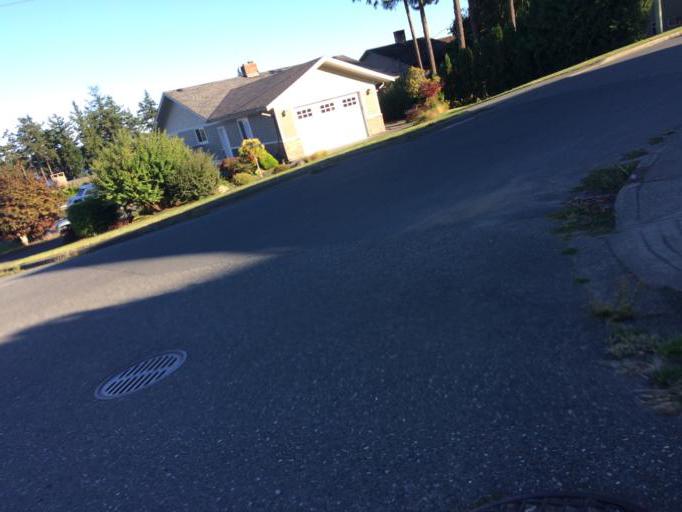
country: CA
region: British Columbia
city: Campbell River
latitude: 50.0040
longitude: -125.2358
